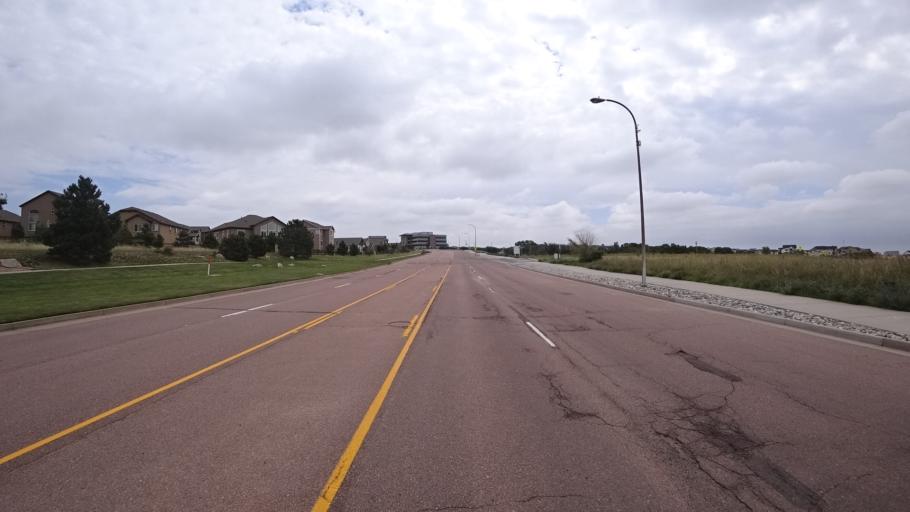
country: US
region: Colorado
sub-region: El Paso County
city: Gleneagle
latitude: 39.0097
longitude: -104.8142
